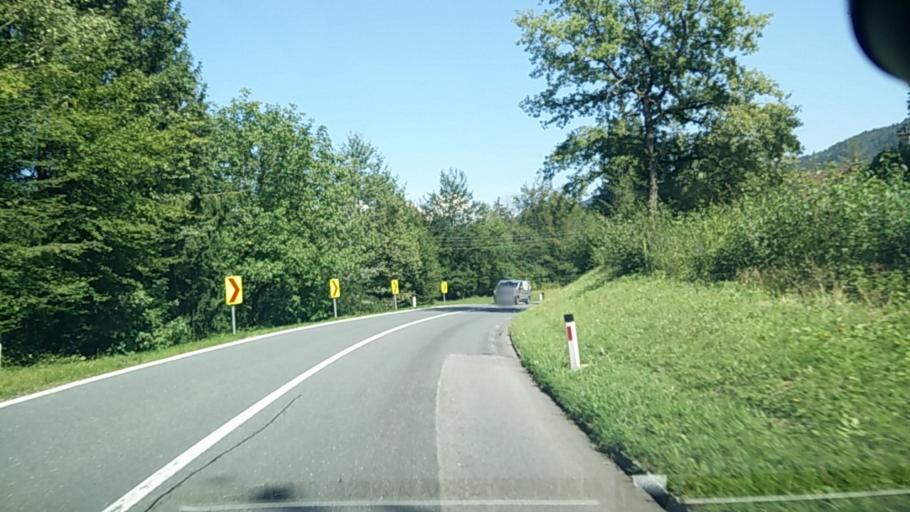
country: AT
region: Carinthia
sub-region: Politischer Bezirk Volkermarkt
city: Sittersdorf
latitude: 46.5380
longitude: 14.5902
